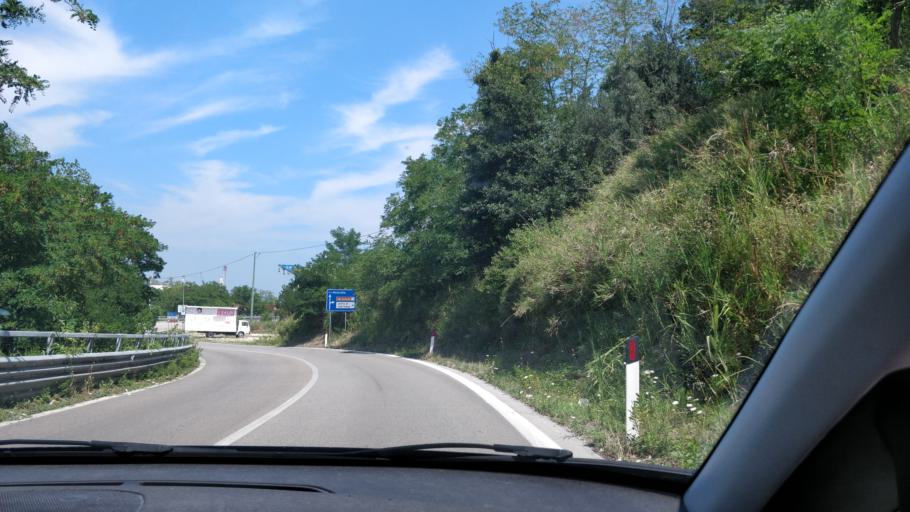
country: IT
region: Abruzzo
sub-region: Provincia di Chieti
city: Ortona
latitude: 42.3435
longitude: 14.4111
